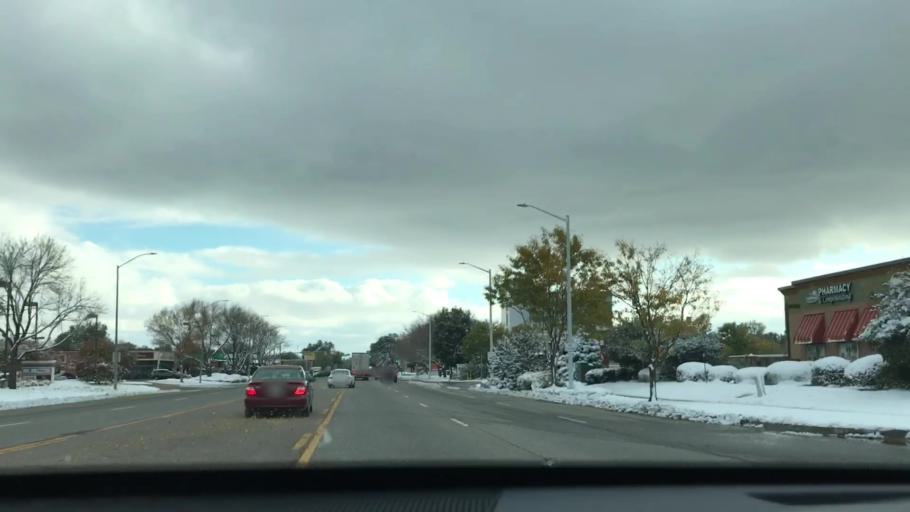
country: US
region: Colorado
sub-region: Boulder County
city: Longmont
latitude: 40.1908
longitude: -105.1024
